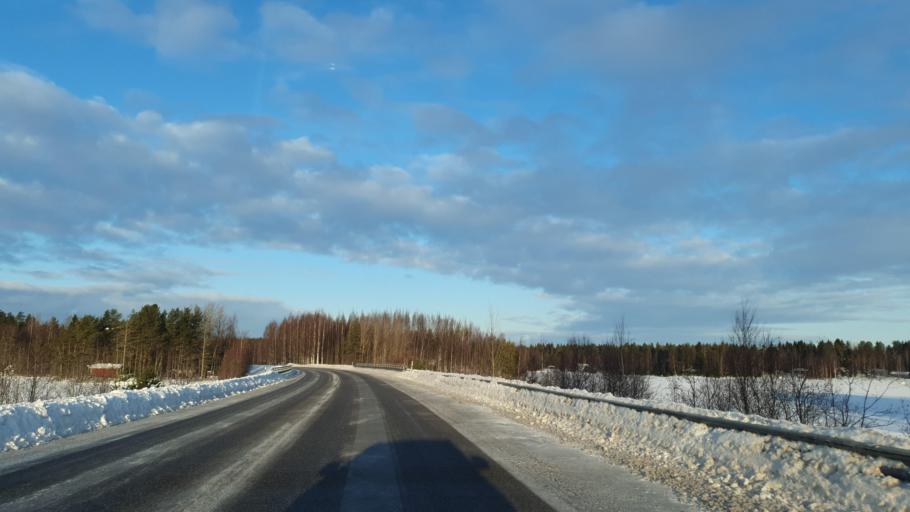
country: FI
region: Kainuu
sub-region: Kajaani
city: Vaala
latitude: 64.5508
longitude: 27.1599
